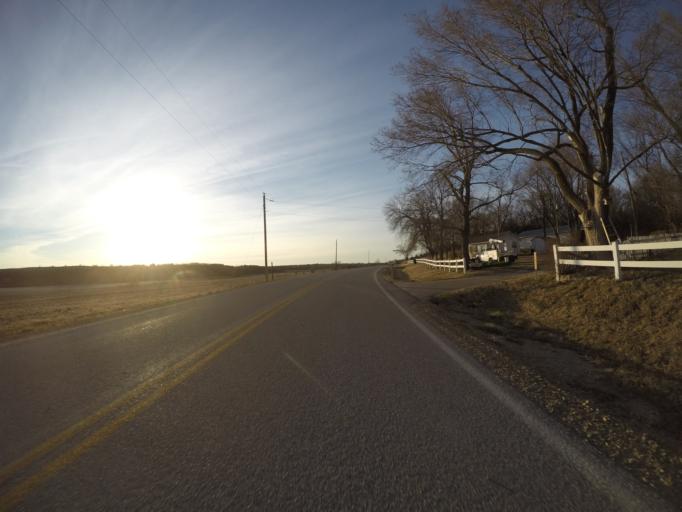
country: US
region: Kansas
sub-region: Riley County
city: Ogden
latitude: 39.3066
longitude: -96.7288
